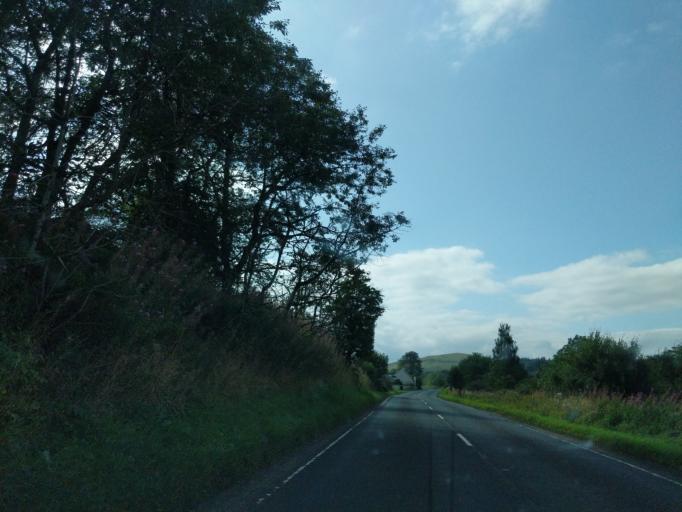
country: GB
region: Scotland
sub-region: The Scottish Borders
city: Peebles
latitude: 55.6938
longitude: -3.2129
